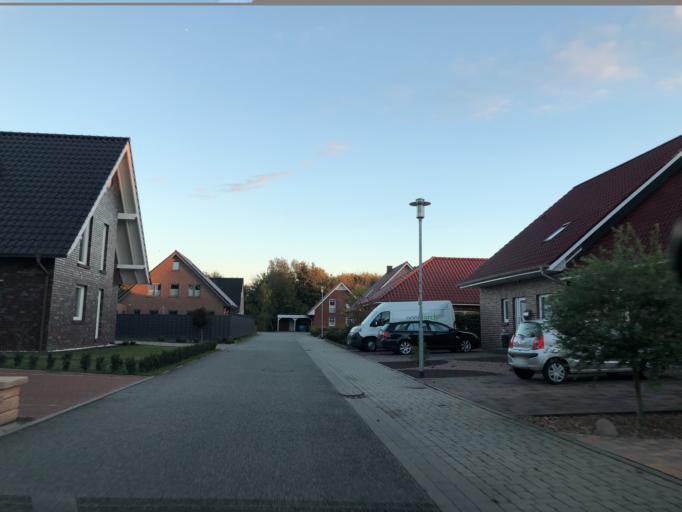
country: DE
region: Lower Saxony
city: Papenburg
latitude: 53.0865
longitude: 7.4103
